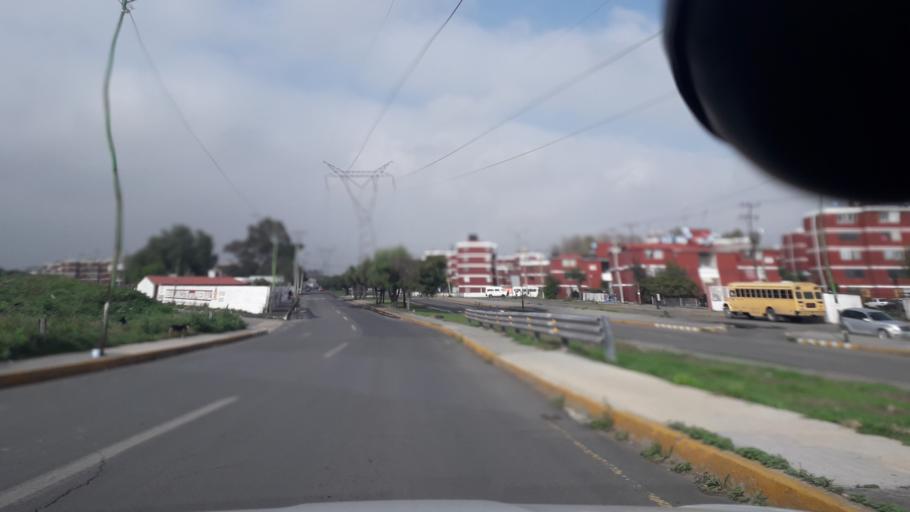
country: MX
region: Mexico
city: Coacalco
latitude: 19.6446
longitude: -99.0817
